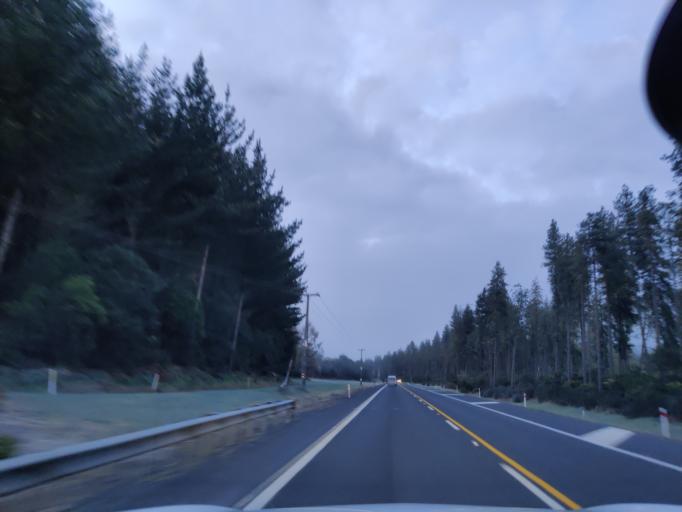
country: NZ
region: Waikato
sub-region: South Waikato District
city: Tokoroa
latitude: -38.3793
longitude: 176.0023
